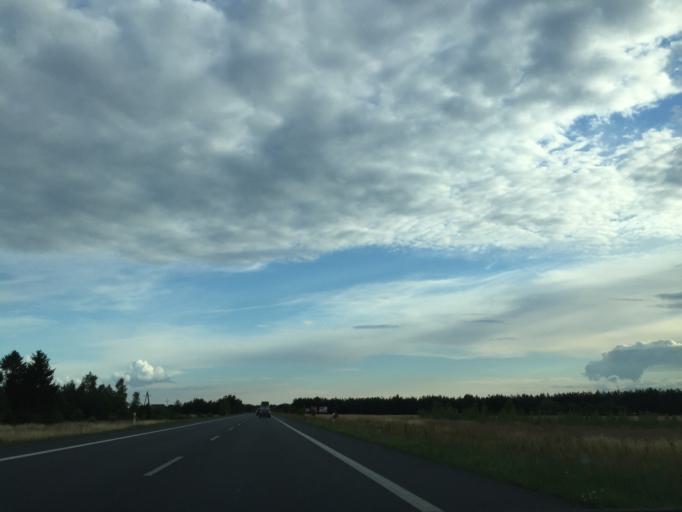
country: PL
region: Lublin Voivodeship
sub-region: Powiat lubartowski
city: Lubartow
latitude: 51.4725
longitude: 22.5846
